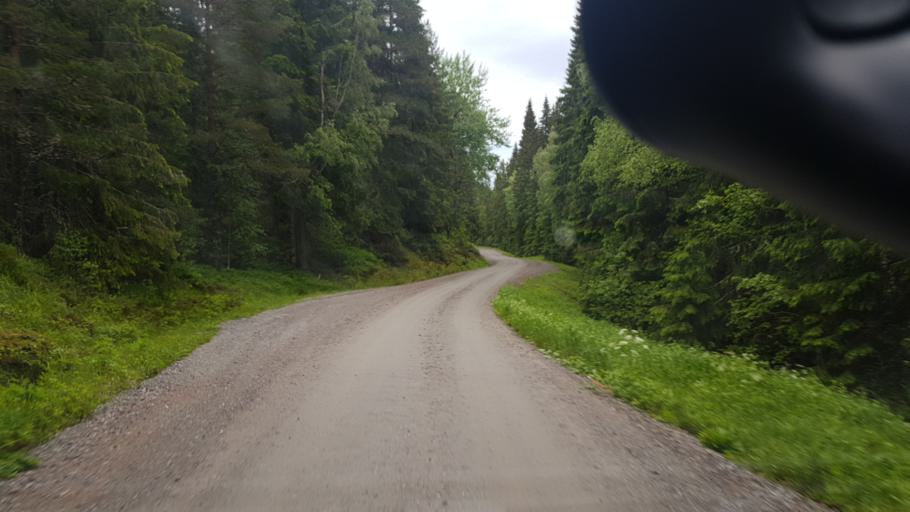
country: NO
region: Ostfold
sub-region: Romskog
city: Romskog
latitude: 59.7128
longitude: 12.0216
